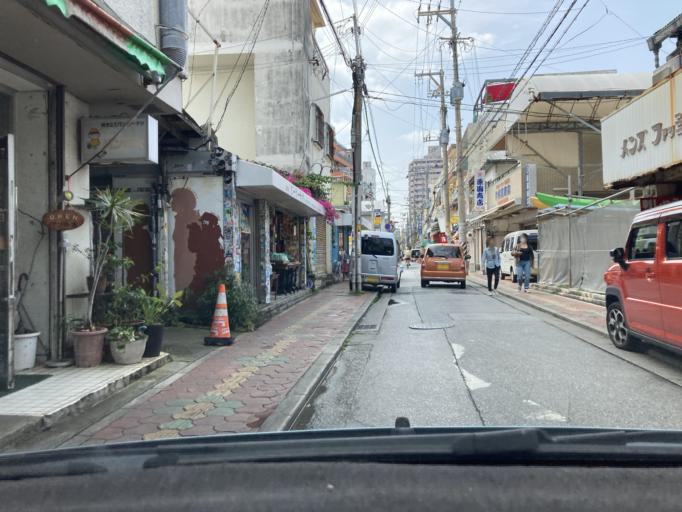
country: JP
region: Okinawa
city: Naha-shi
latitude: 26.2134
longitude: 127.6892
